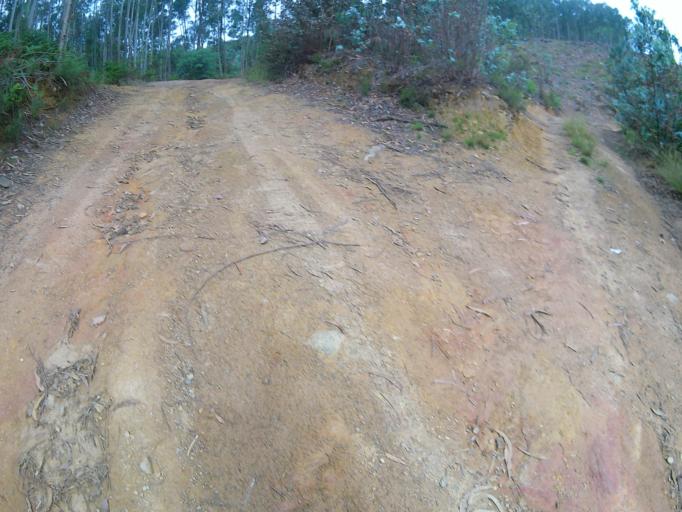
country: PT
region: Aveiro
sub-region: Albergaria-A-Velha
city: Branca
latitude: 40.7577
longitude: -8.4276
